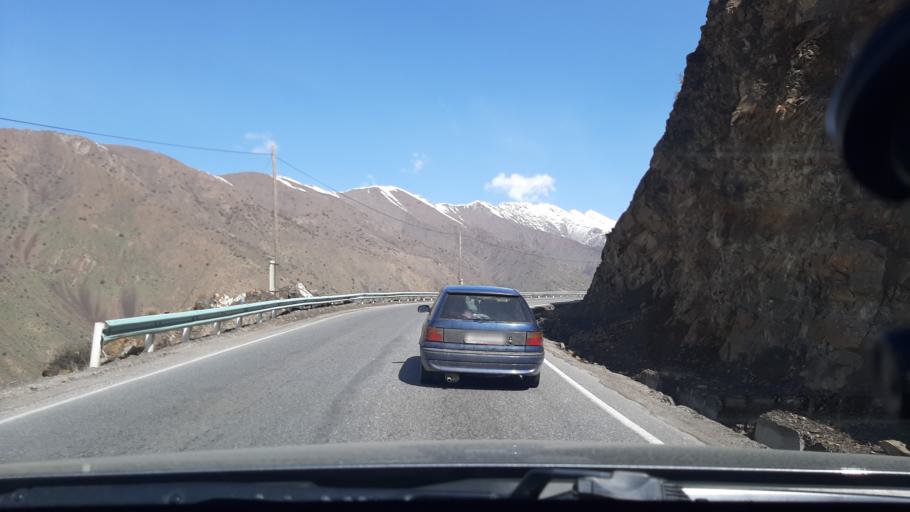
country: TJ
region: Viloyati Sughd
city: Ayni
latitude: 39.4481
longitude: 68.5502
